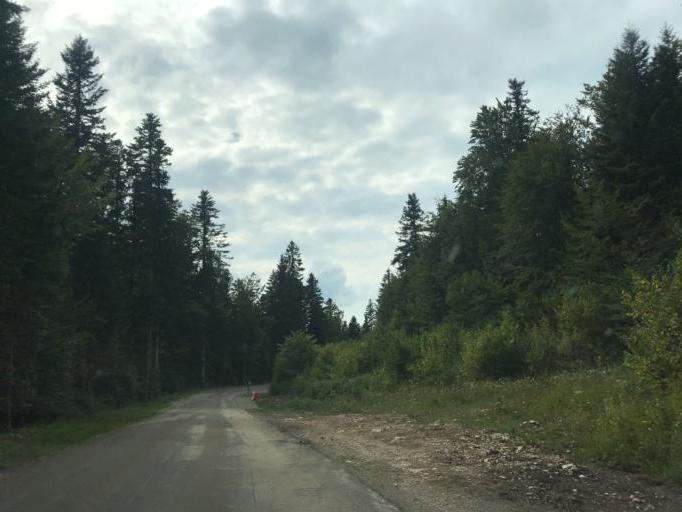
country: FR
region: Franche-Comte
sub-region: Departement du Jura
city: Longchaumois
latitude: 46.5064
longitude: 5.8878
